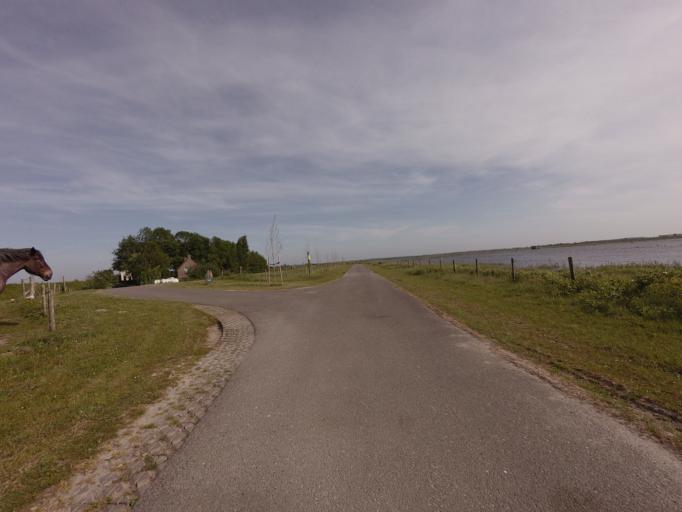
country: NL
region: South Holland
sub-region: Gemeente Spijkenisse
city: Spijkenisse
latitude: 51.7400
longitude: 4.3337
